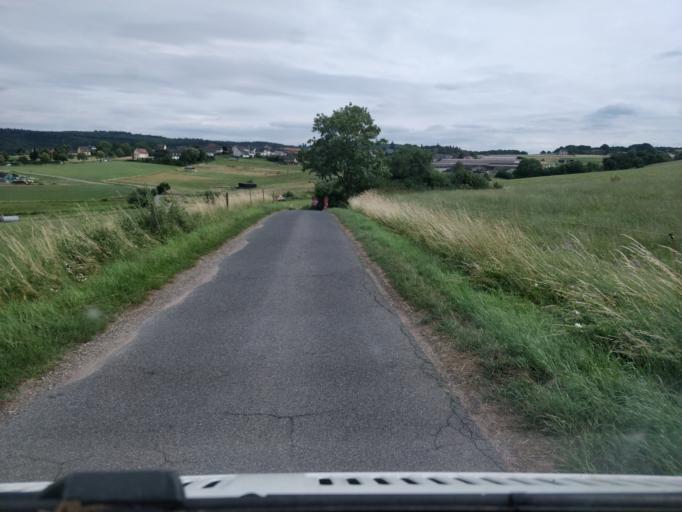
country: DE
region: North Rhine-Westphalia
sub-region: Regierungsbezirk Koln
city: Rheinbach
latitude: 50.5981
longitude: 6.9266
